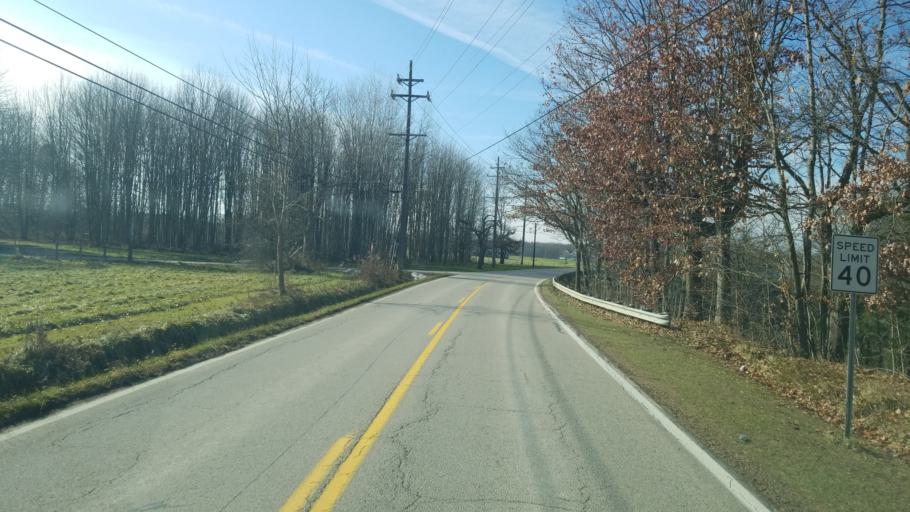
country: US
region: Ohio
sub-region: Ashtabula County
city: Jefferson
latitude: 41.7163
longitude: -80.8304
